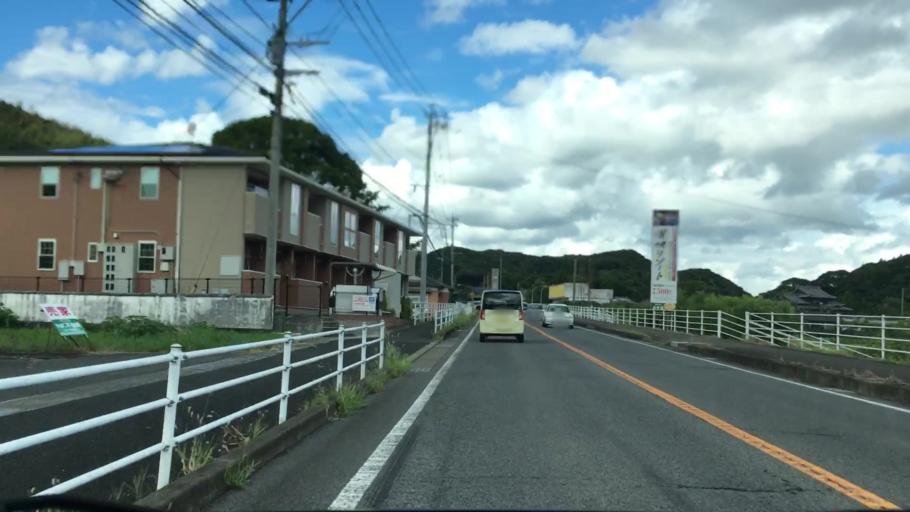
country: JP
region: Nagasaki
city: Sasebo
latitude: 33.1600
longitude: 129.8318
